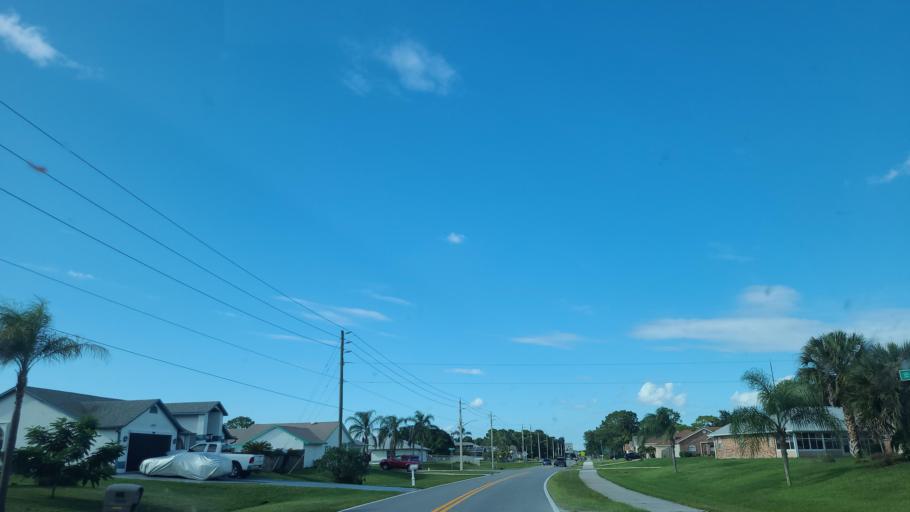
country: US
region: Florida
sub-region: Brevard County
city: Grant-Valkaria
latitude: 27.9572
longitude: -80.6609
